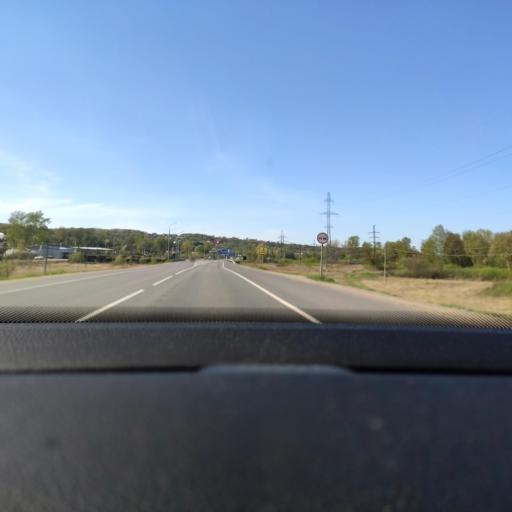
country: RU
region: Moskovskaya
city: Yakhroma
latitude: 56.3000
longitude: 37.4834
